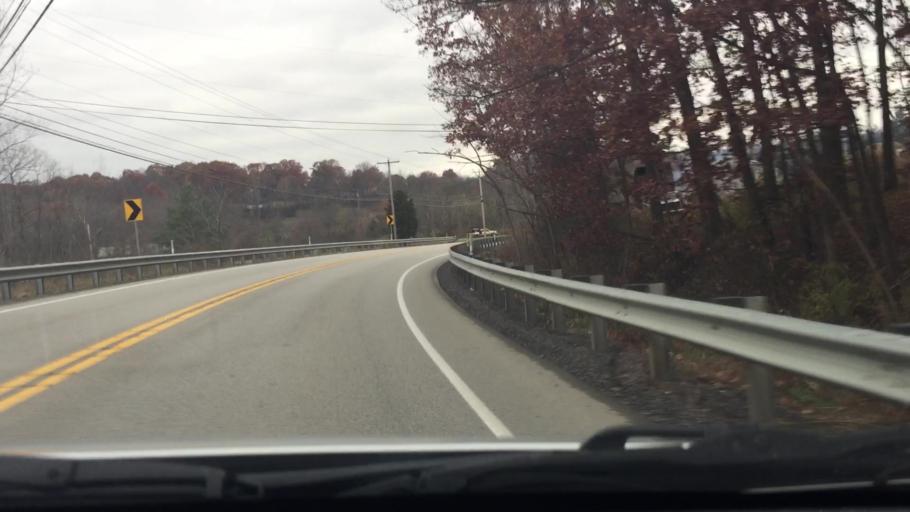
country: US
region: Pennsylvania
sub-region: Butler County
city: Nixon
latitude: 40.7205
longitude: -79.8927
